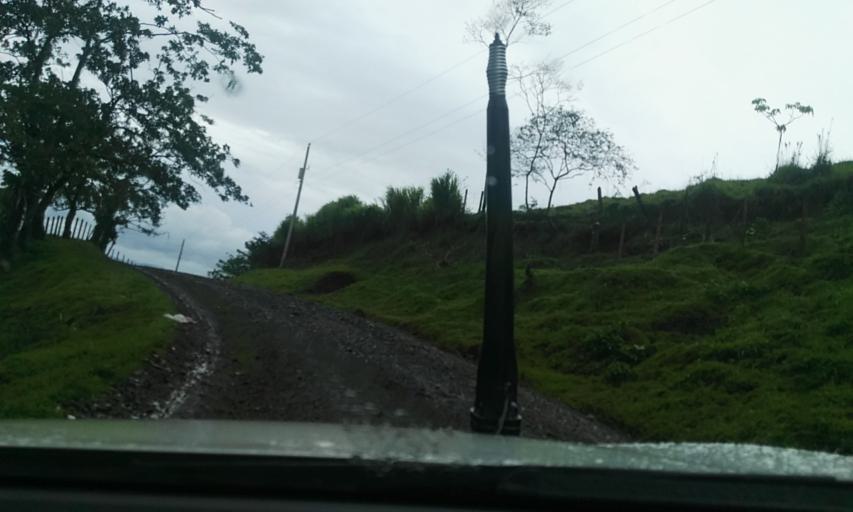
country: NI
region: Matagalpa
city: Rio Blanco
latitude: 13.0183
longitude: -85.2075
